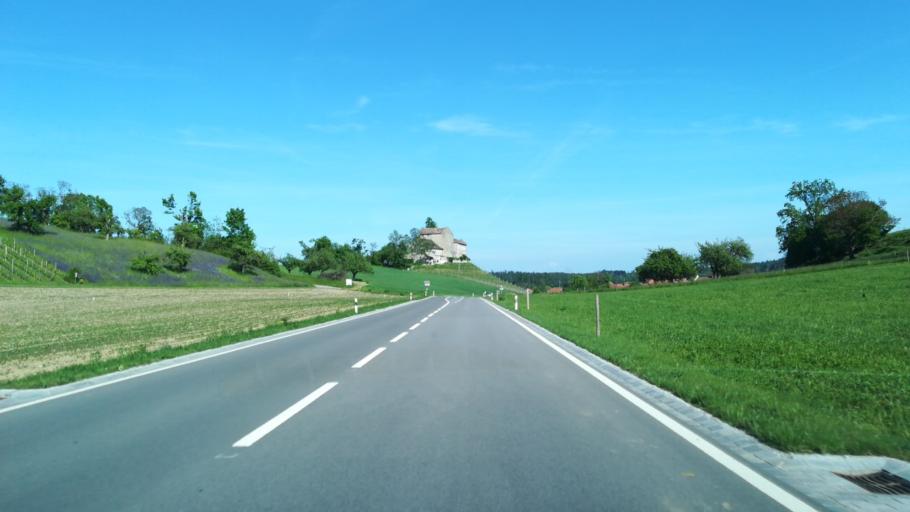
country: CH
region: Thurgau
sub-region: Frauenfeld District
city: Diessenhofen
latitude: 47.6243
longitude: 8.7718
